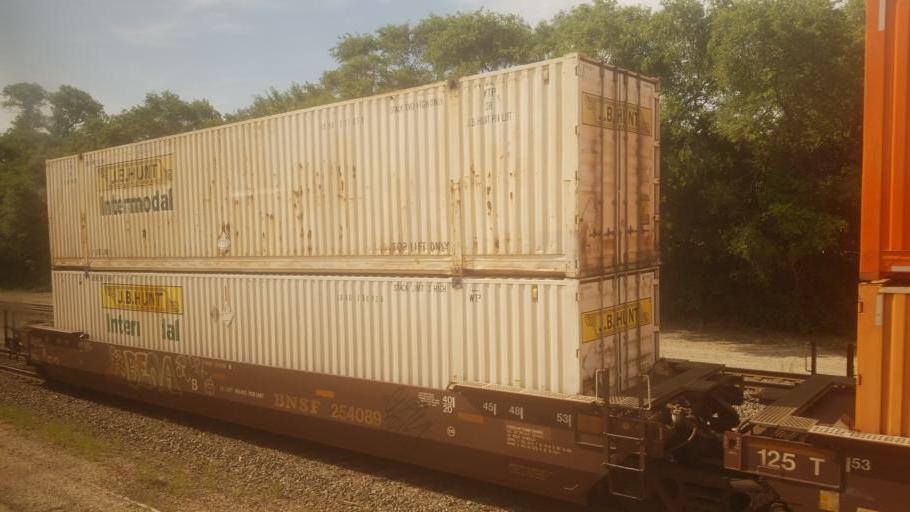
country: US
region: Kansas
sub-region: Johnson County
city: Roeland Park
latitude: 39.0763
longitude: -94.6590
